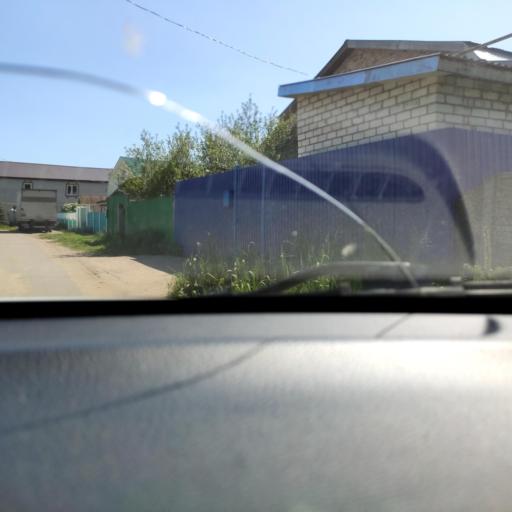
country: RU
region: Tatarstan
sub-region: Gorod Kazan'
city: Kazan
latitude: 55.8601
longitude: 49.1980
